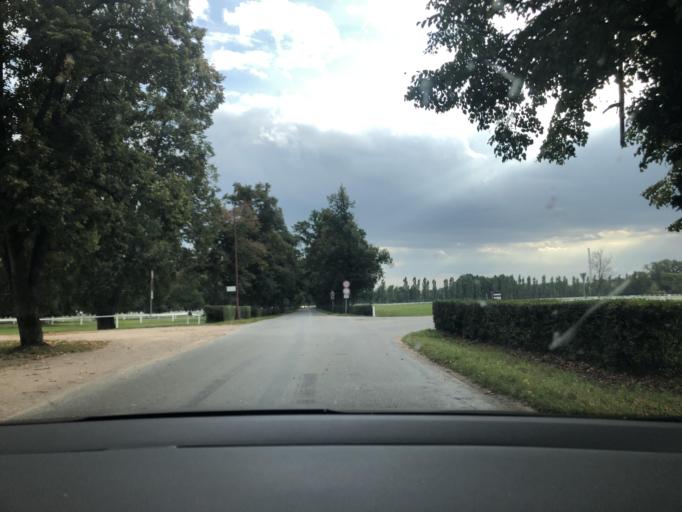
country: CZ
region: Pardubicky
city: Recany nad Labem
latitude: 50.0576
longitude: 15.4824
